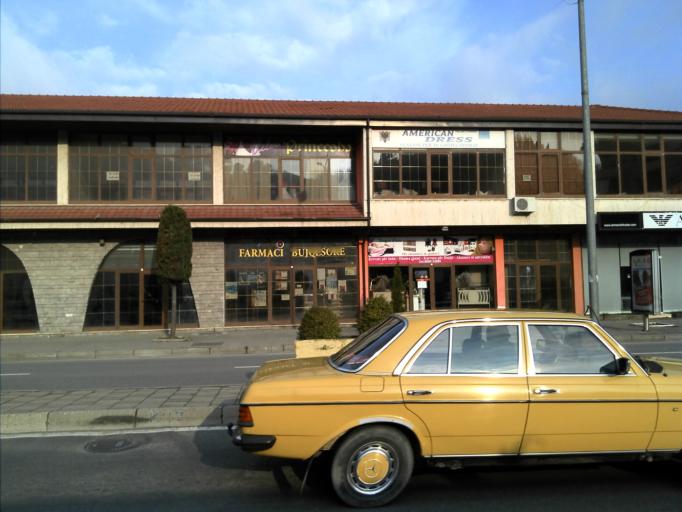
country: AL
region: Shkoder
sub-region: Rrethi i Shkodres
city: Shkoder
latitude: 42.0534
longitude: 19.4977
